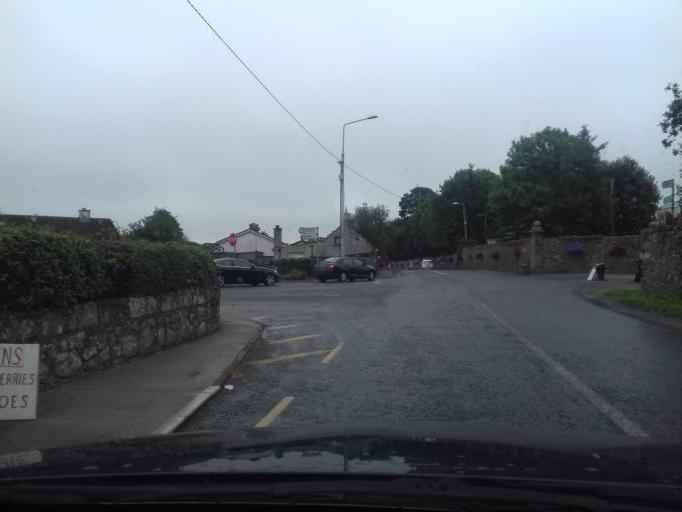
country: IE
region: Leinster
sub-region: Kilkenny
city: Graiguenamanagh
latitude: 52.6039
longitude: -6.9372
